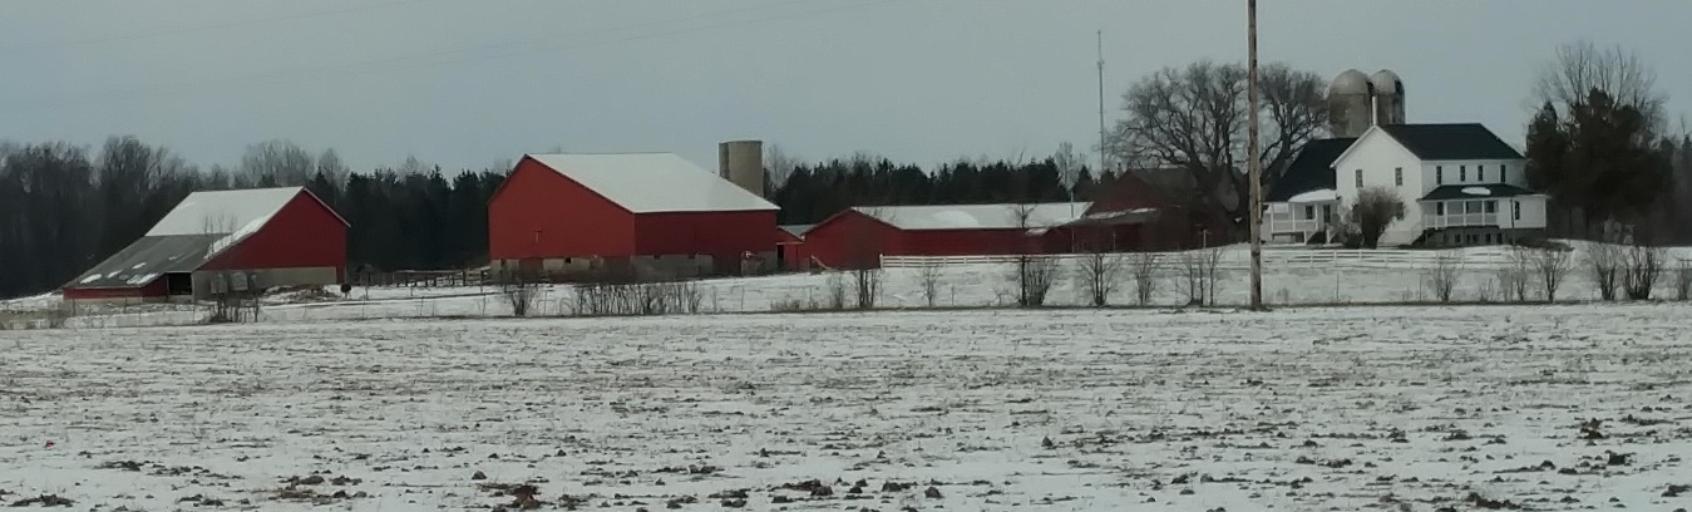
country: US
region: Michigan
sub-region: Gladwin County
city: Gladwin
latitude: 44.0324
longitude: -84.4673
